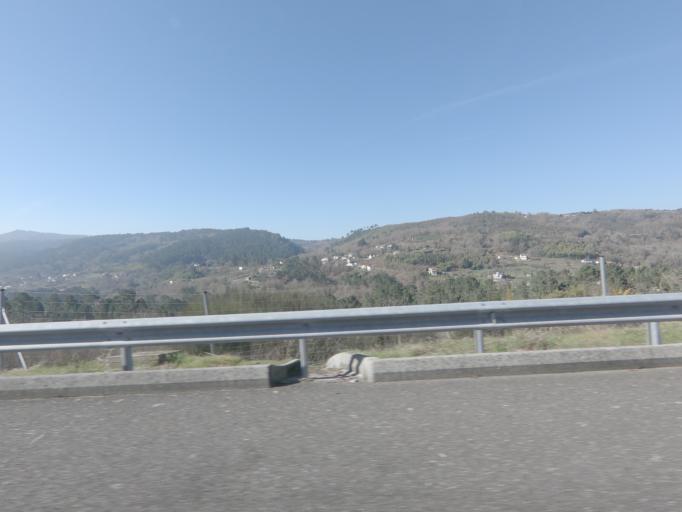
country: ES
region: Galicia
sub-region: Provincia de Ourense
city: Punxin
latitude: 42.3838
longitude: -7.9893
